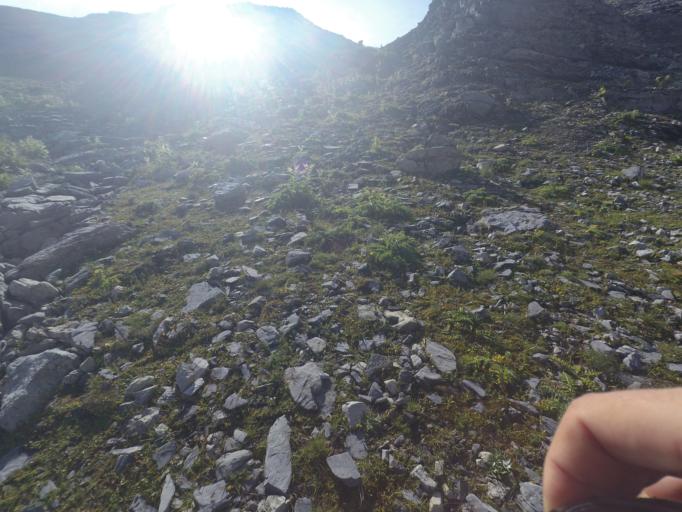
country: AT
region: Salzburg
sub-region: Politischer Bezirk Sankt Johann im Pongau
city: Kleinarl
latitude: 47.2231
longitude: 13.4099
